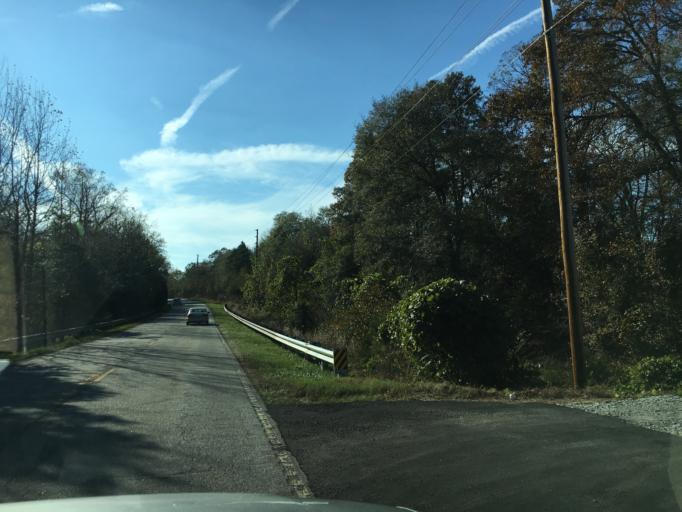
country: US
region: South Carolina
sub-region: Anderson County
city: Iva
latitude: 34.3297
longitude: -82.7818
